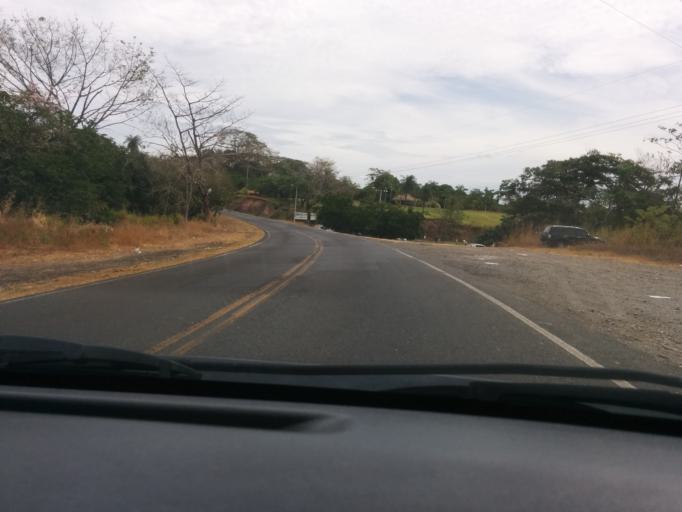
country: CR
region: Puntarenas
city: Esparza
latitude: 10.0024
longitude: -84.6212
